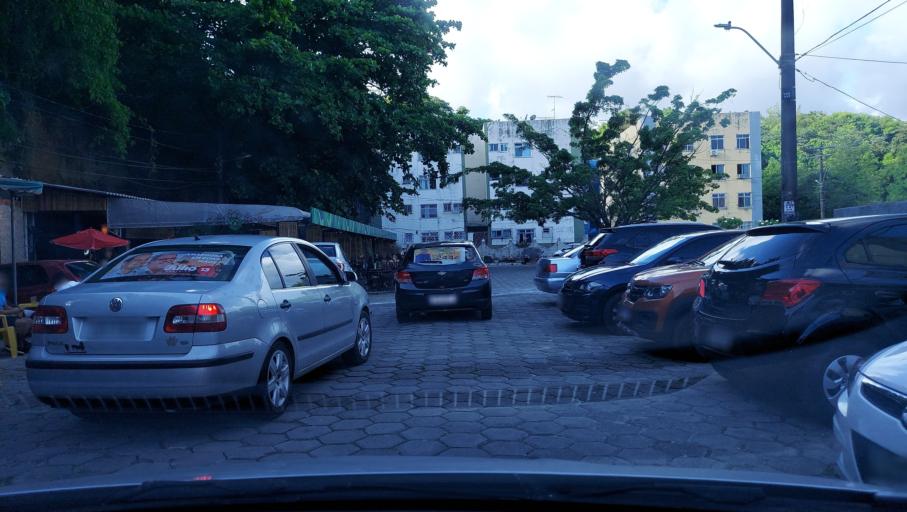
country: BR
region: Bahia
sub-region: Salvador
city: Salvador
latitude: -12.9793
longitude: -38.4452
